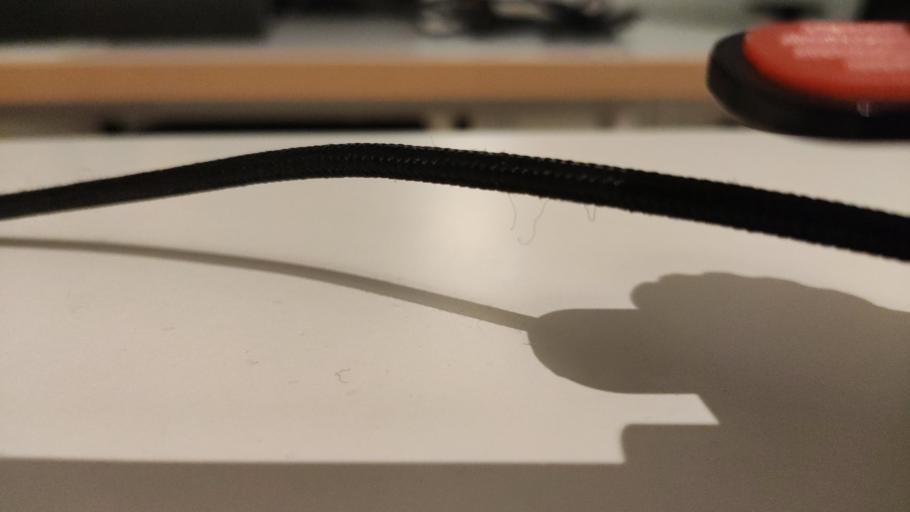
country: RU
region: Moskovskaya
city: Novosin'kovo
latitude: 56.4012
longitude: 37.2549
